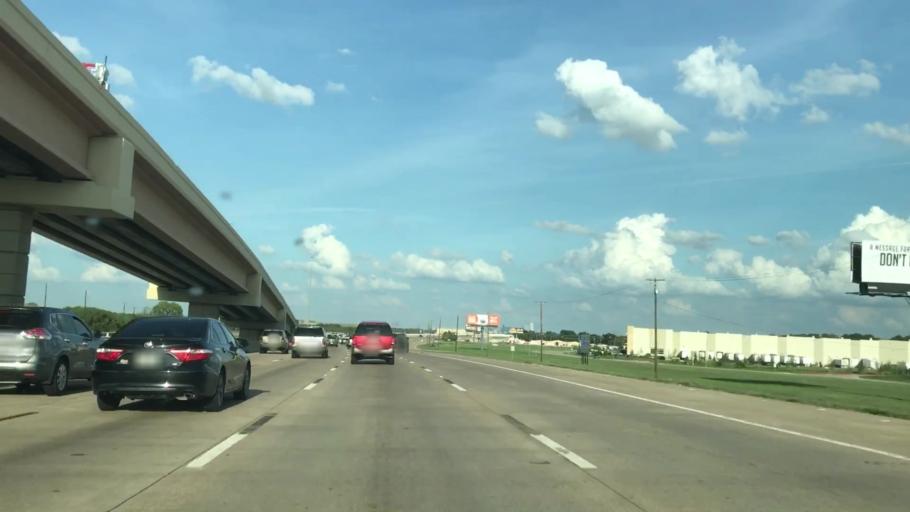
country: US
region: Texas
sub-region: Dallas County
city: Grand Prairie
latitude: 32.7600
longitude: -96.9709
